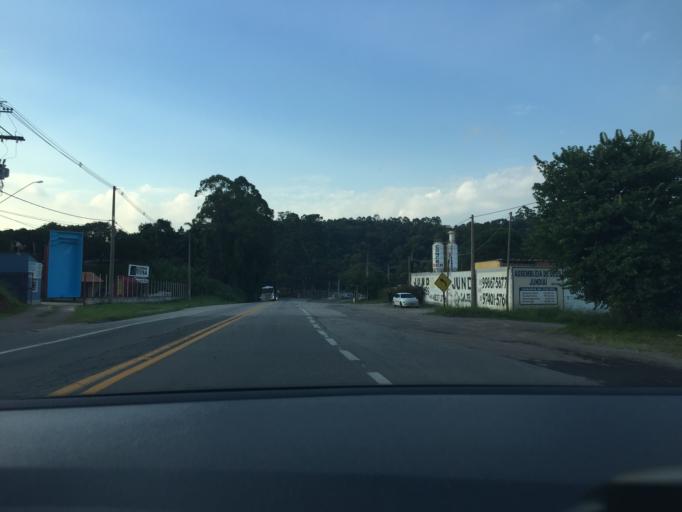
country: BR
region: Sao Paulo
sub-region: Varzea Paulista
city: Varzea Paulista
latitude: -23.2514
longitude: -46.8379
